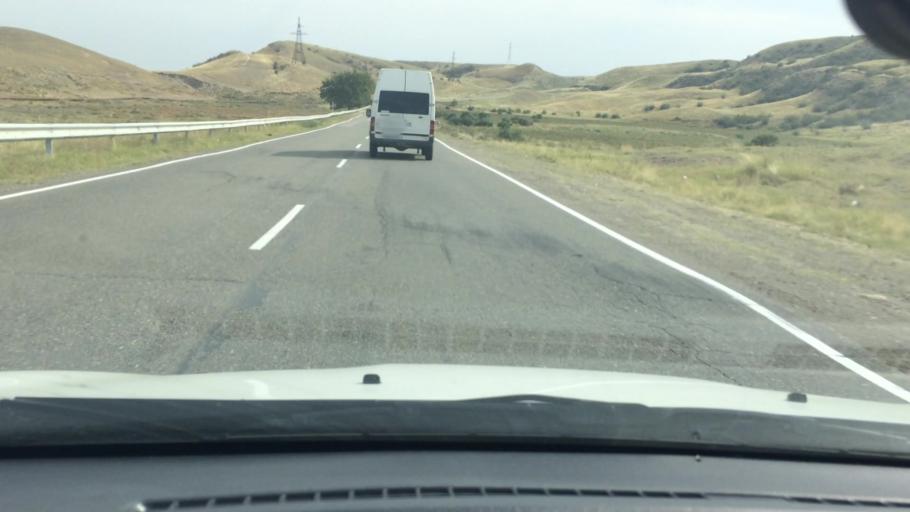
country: GE
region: Kvemo Kartli
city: Rust'avi
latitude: 41.5307
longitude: 44.9849
